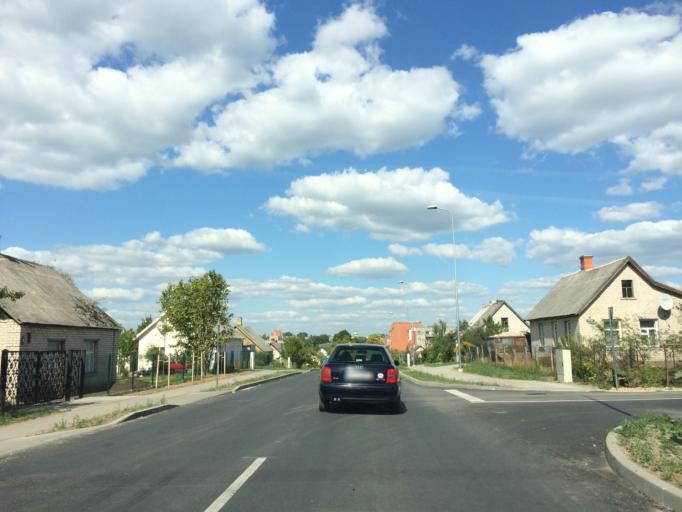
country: LV
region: Rezekne
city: Rezekne
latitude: 56.5131
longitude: 27.3445
